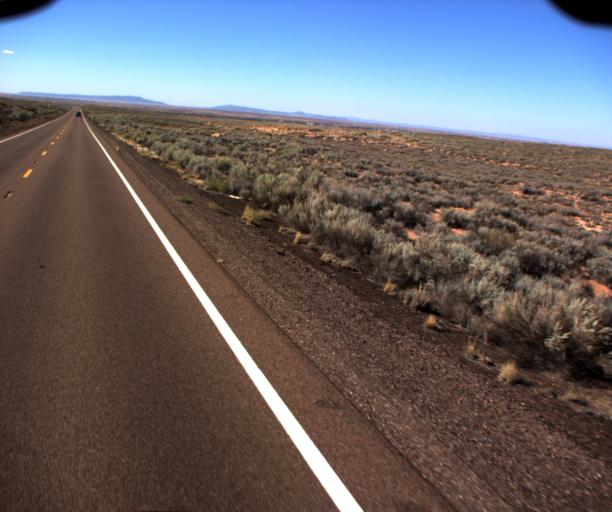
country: US
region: Arizona
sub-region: Navajo County
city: Winslow
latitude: 35.0324
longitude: -110.6200
